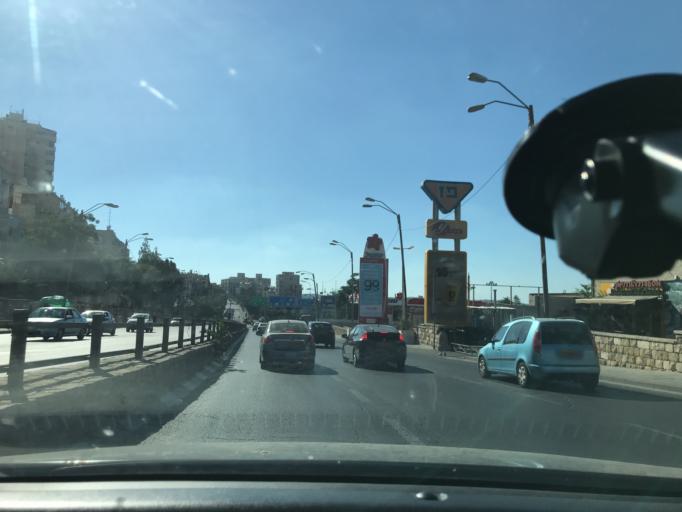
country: IL
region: Jerusalem
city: West Jerusalem
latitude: 31.7895
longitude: 35.1993
